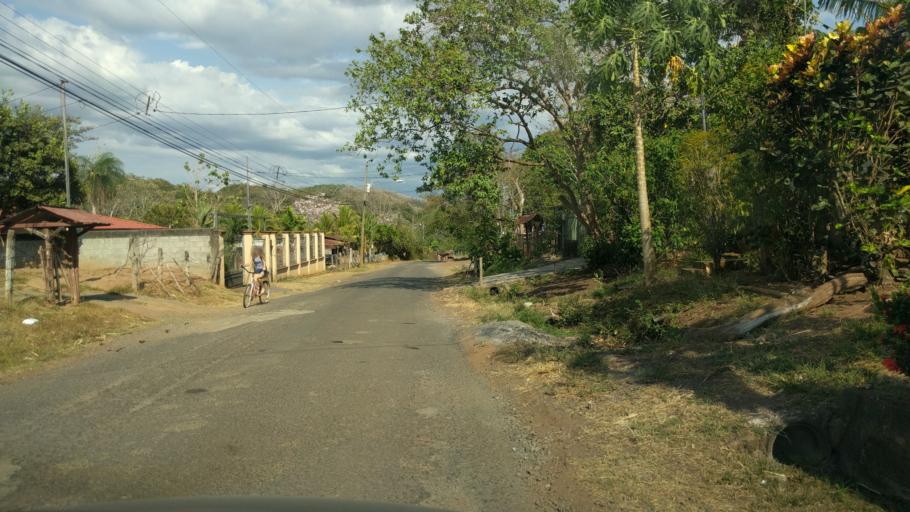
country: CR
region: Puntarenas
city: Esparza
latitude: 10.0142
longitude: -84.6932
